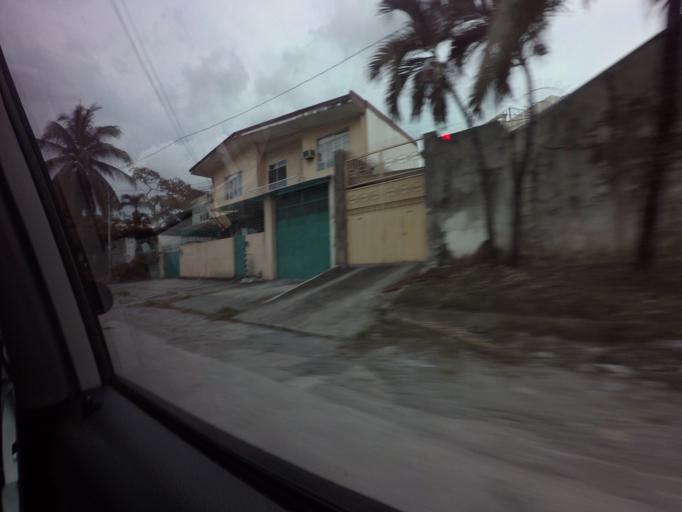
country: PH
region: Calabarzon
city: Del Monte
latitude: 14.6193
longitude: 121.0054
